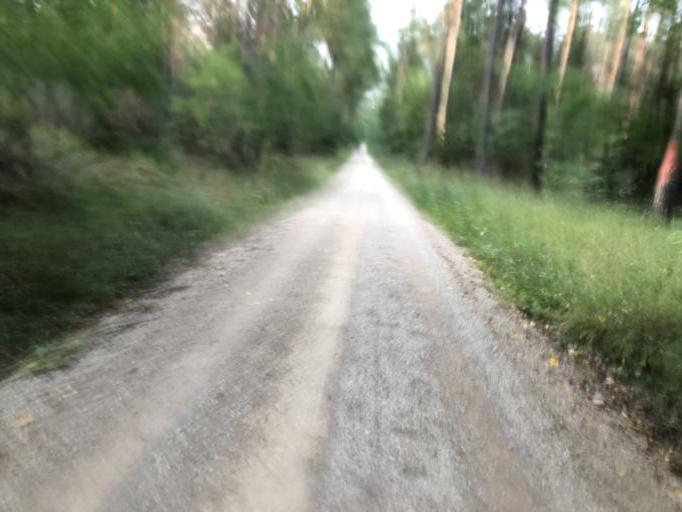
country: DE
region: Bavaria
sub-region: Regierungsbezirk Mittelfranken
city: Uttenreuth
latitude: 49.5708
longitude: 11.0757
